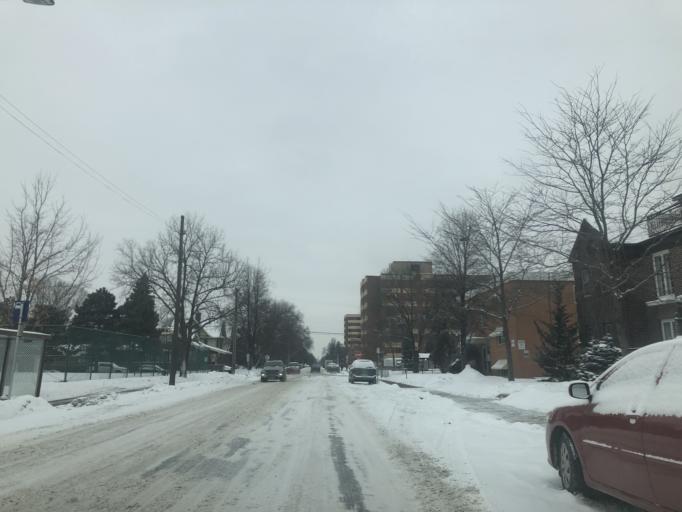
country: US
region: Minnesota
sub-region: Hennepin County
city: Richfield
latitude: 44.9333
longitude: -93.2908
